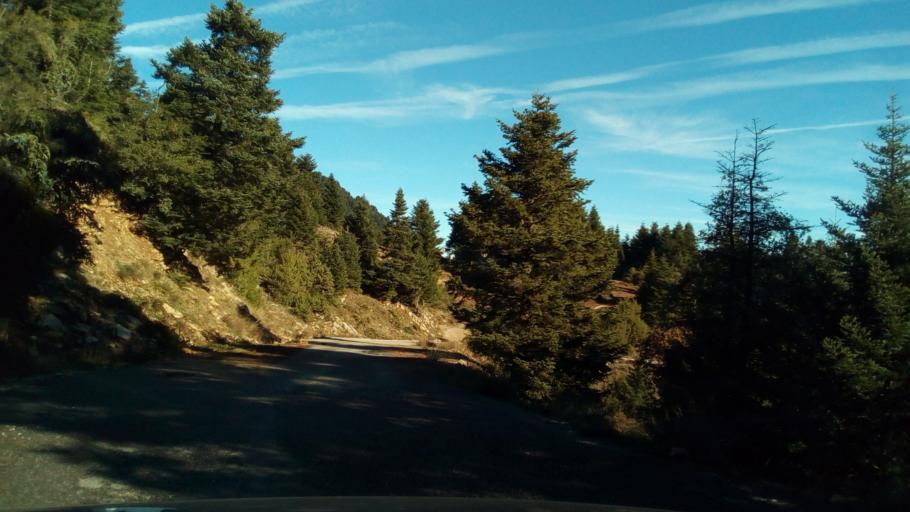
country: GR
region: West Greece
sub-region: Nomos Aitolias kai Akarnanias
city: Nafpaktos
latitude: 38.5353
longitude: 21.8420
